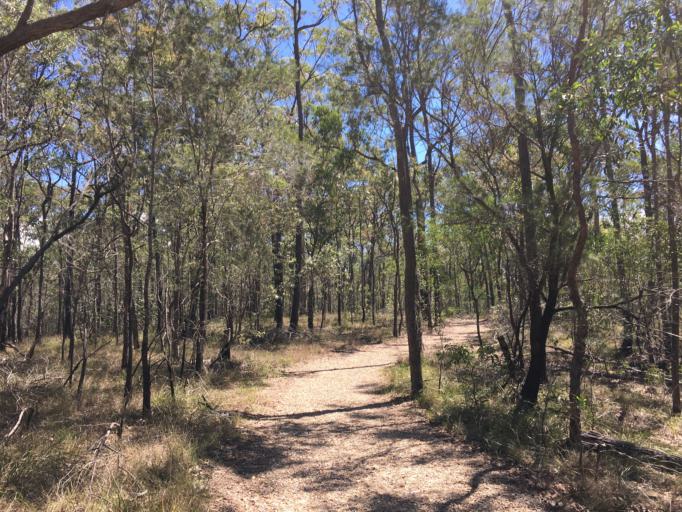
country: AU
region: Queensland
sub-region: Logan
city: Woodridge
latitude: -27.6268
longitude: 153.0884
